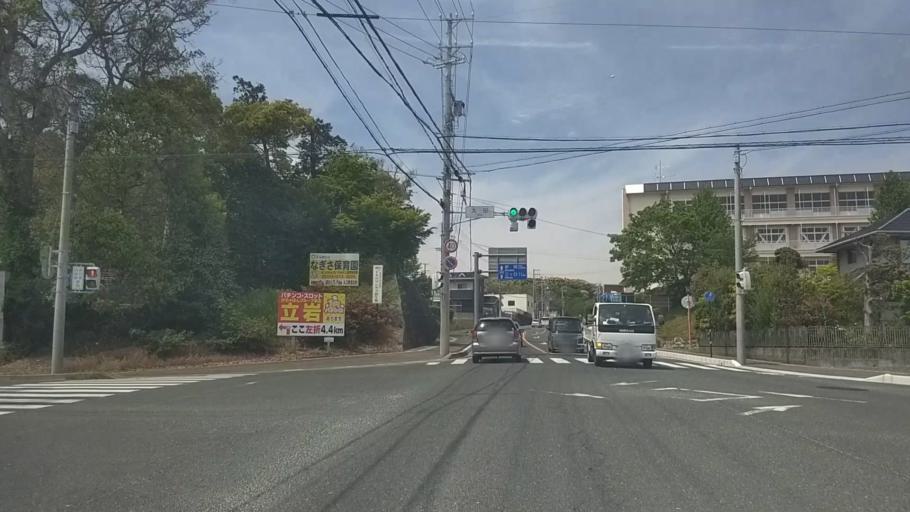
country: JP
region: Shizuoka
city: Kosai-shi
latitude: 34.7412
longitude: 137.5158
